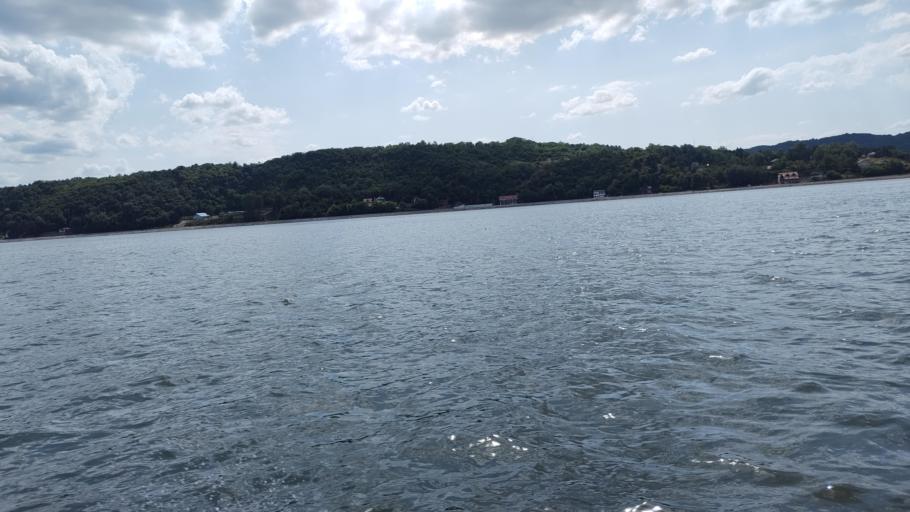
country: RS
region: Central Serbia
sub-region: Branicevski Okrug
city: Golubac
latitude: 44.6653
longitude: 21.6231
